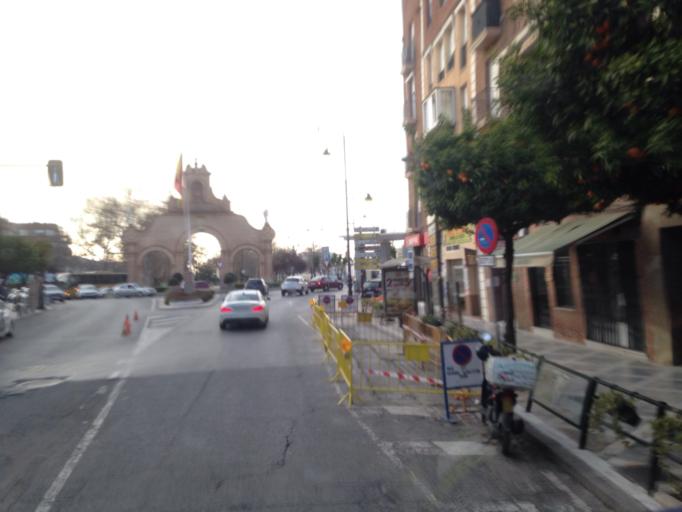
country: ES
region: Andalusia
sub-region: Provincia de Malaga
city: Antequera
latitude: 37.0215
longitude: -4.5650
